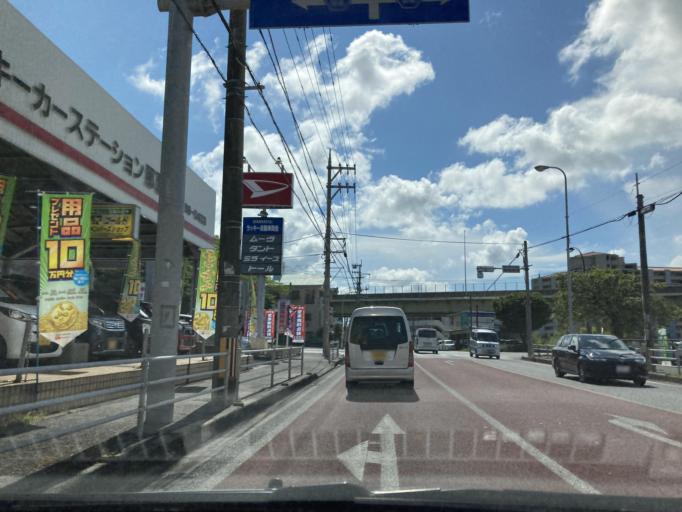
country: JP
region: Okinawa
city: Tomigusuku
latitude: 26.1809
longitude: 127.7160
